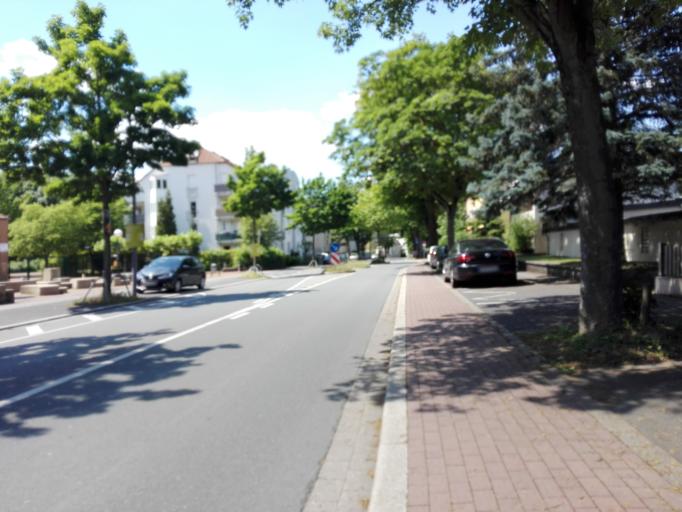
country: DE
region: North Rhine-Westphalia
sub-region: Regierungsbezirk Arnsberg
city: Unna
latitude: 51.5354
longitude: 7.6990
